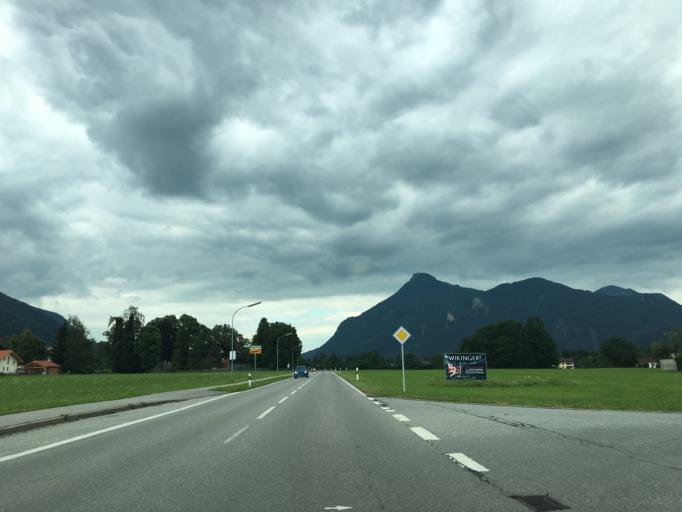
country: DE
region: Bavaria
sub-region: Upper Bavaria
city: Oberaudorf
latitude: 47.6526
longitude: 12.1728
